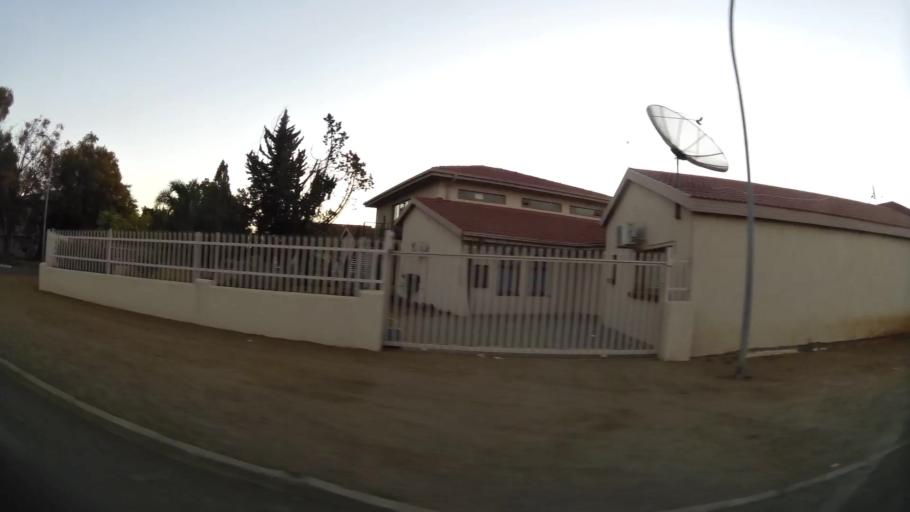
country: ZA
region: Northern Cape
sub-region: Frances Baard District Municipality
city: Kimberley
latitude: -28.7224
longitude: 24.7761
